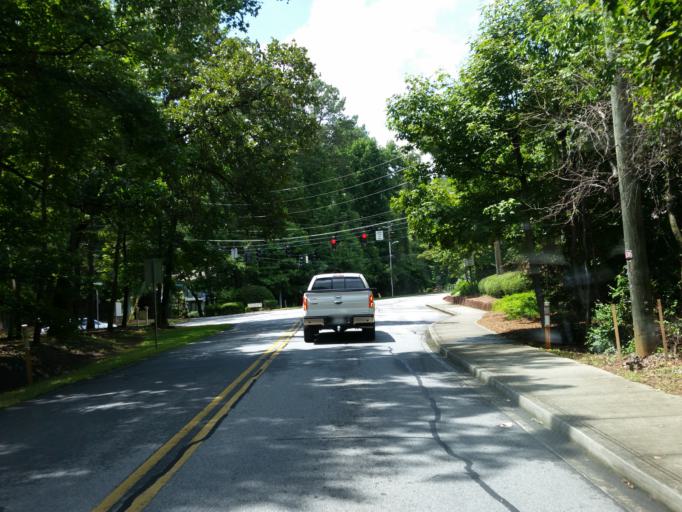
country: US
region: Georgia
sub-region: DeKalb County
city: Dunwoody
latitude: 33.9624
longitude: -84.3464
